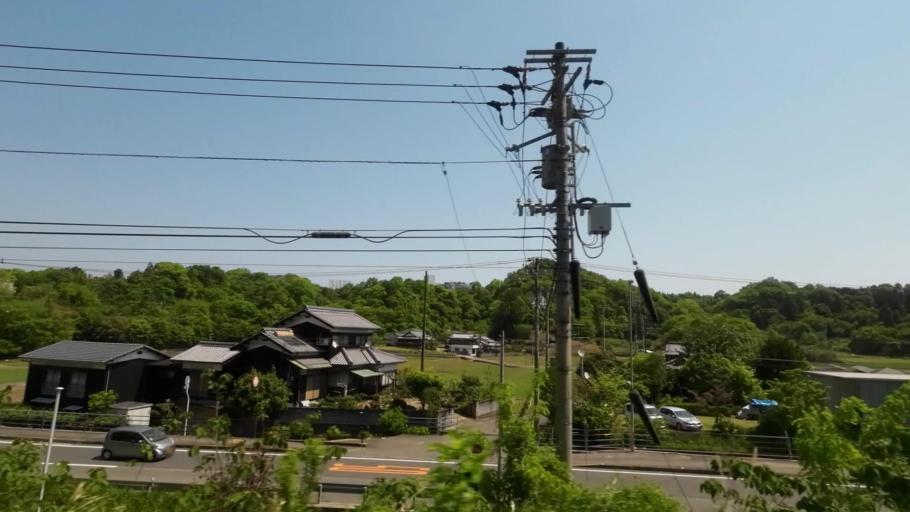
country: JP
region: Ehime
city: Saijo
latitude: 33.9916
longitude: 133.0507
